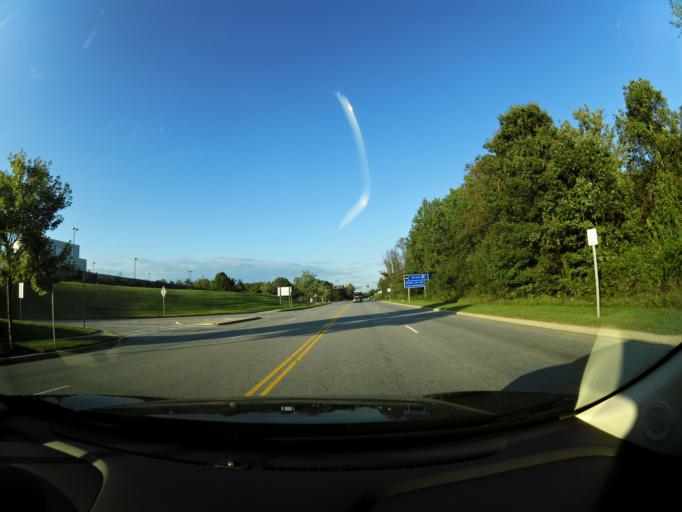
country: US
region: Maryland
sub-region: Howard County
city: Hanover
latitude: 39.1786
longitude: -76.7002
